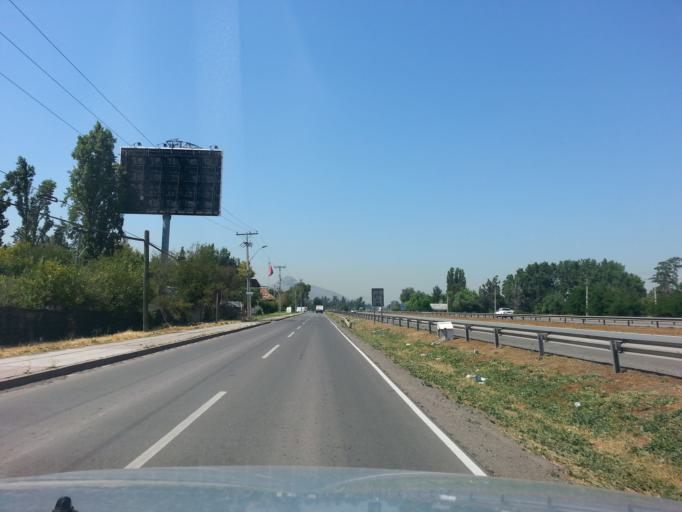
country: CL
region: Santiago Metropolitan
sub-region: Provincia de Chacabuco
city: Chicureo Abajo
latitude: -33.2513
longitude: -70.6977
